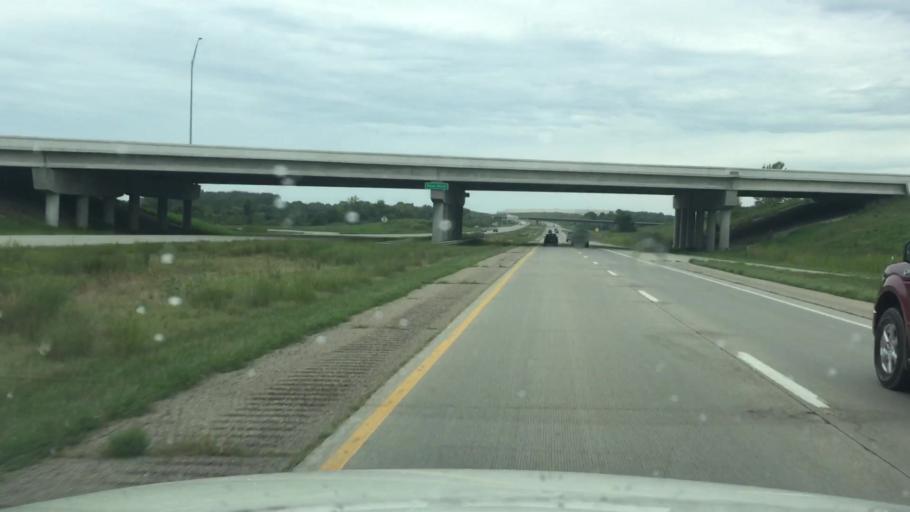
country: US
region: Iowa
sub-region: Warren County
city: Norwalk
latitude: 41.5073
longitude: -93.6440
